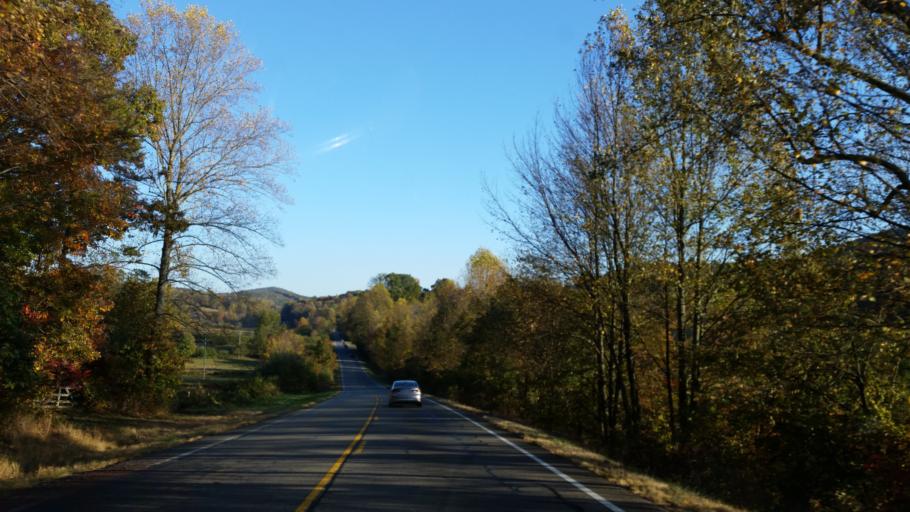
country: US
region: Georgia
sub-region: Gilmer County
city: Ellijay
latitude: 34.6083
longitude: -84.3542
